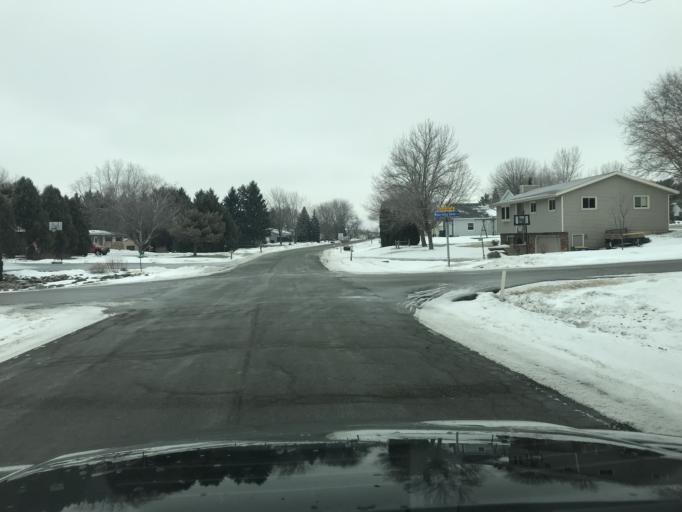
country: US
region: Wisconsin
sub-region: Dane County
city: Cottage Grove
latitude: 43.0961
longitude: -89.2162
